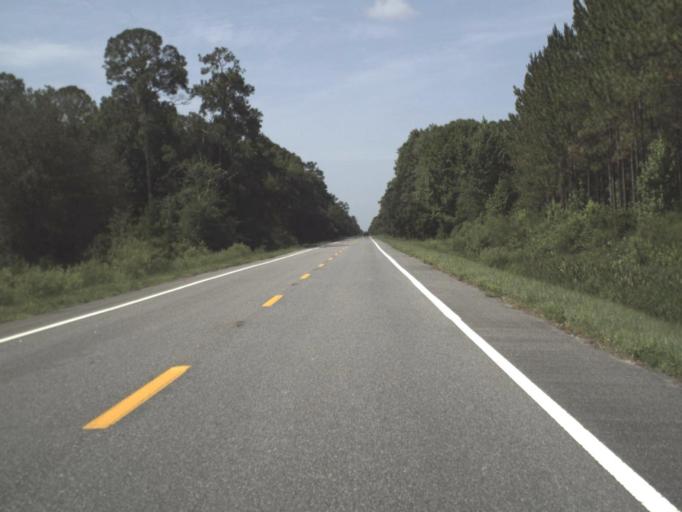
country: US
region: Florida
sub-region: Taylor County
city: Steinhatchee
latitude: 29.8554
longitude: -83.3093
